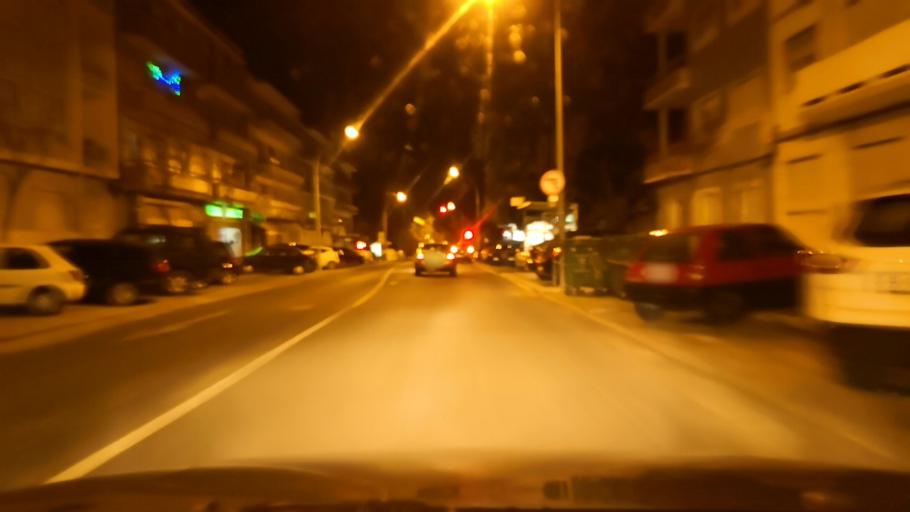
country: PT
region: Setubal
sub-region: Setubal
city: Setubal
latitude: 38.5357
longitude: -8.8937
